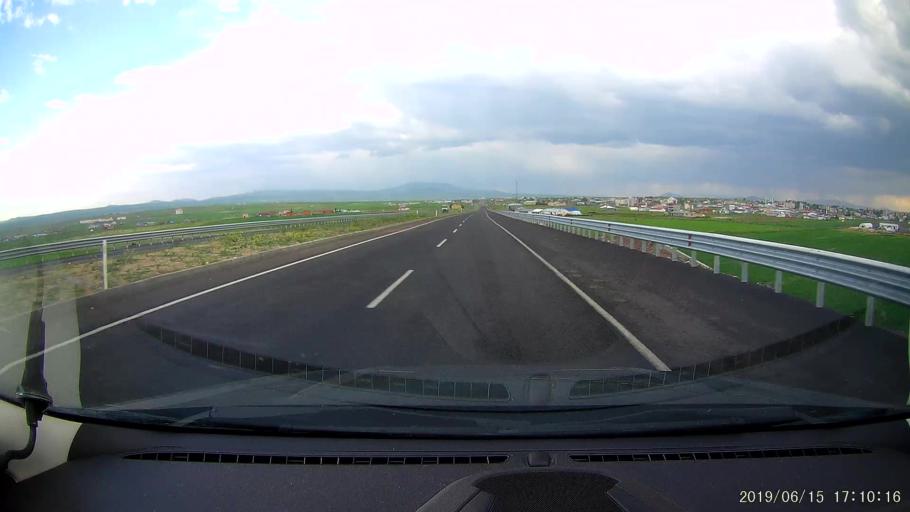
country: TR
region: Kars
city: Kars
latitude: 40.6241
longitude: 43.1338
